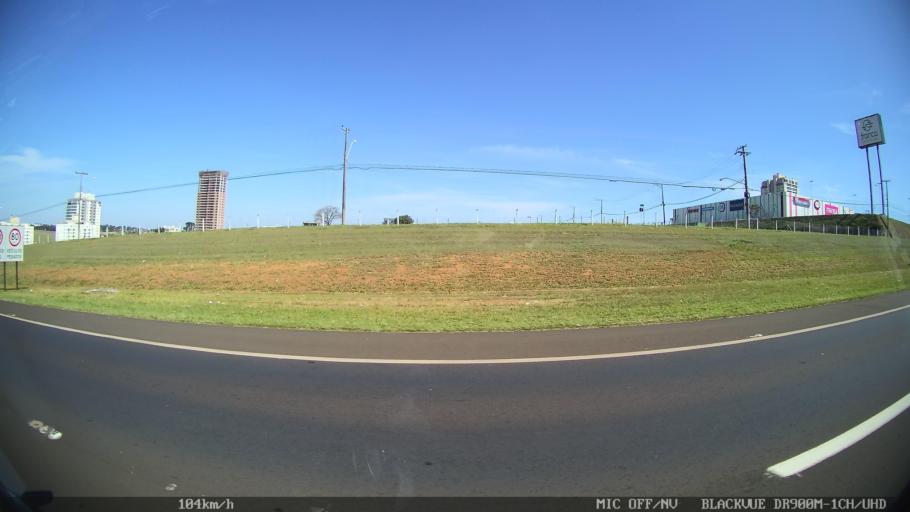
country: BR
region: Sao Paulo
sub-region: Franca
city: Franca
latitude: -20.5483
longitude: -47.4144
